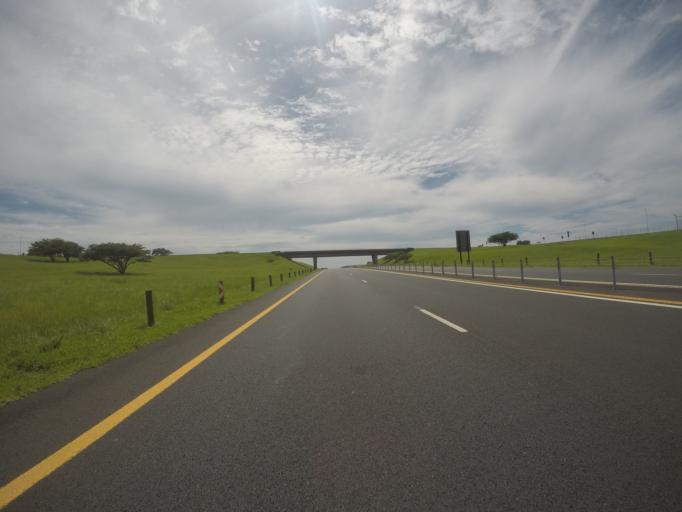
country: ZA
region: KwaZulu-Natal
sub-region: iLembe District Municipality
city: Mandeni
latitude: -29.1847
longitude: 31.4814
